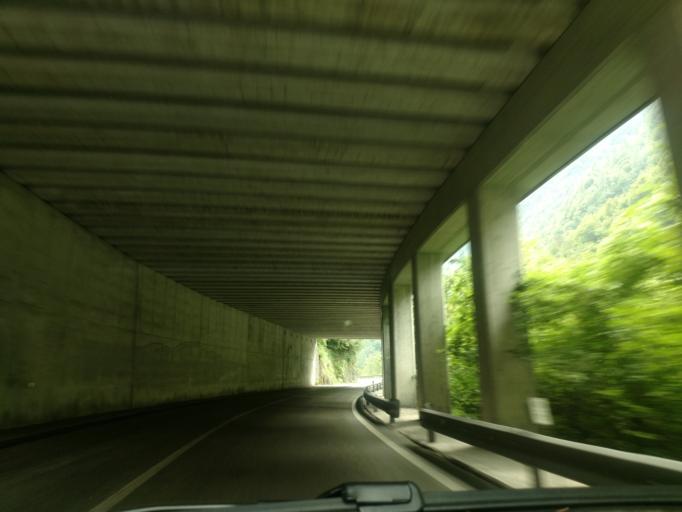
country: IT
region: Veneto
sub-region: Provincia di Belluno
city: Longarone
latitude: 46.2889
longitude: 12.2403
